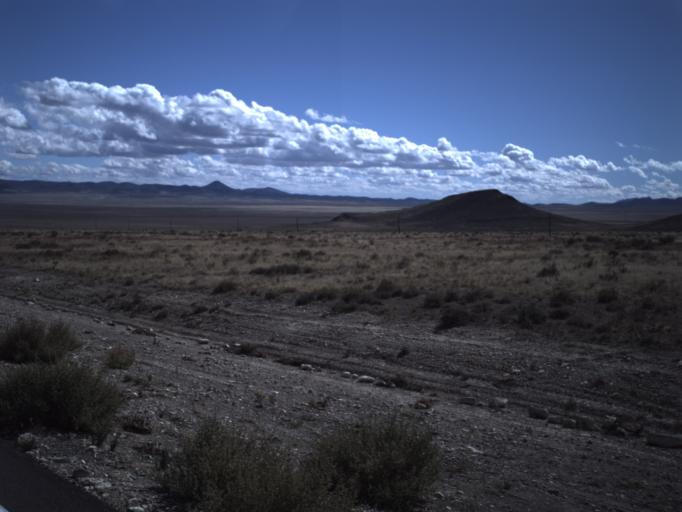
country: US
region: Utah
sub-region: Beaver County
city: Milford
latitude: 38.4930
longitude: -113.4763
